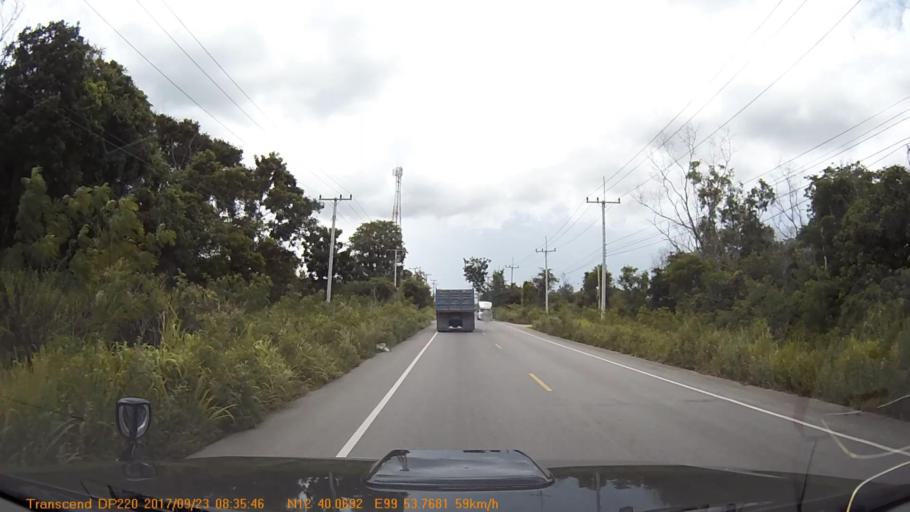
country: TH
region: Prachuap Khiri Khan
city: Hua Hin
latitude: 12.6678
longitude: 99.8961
